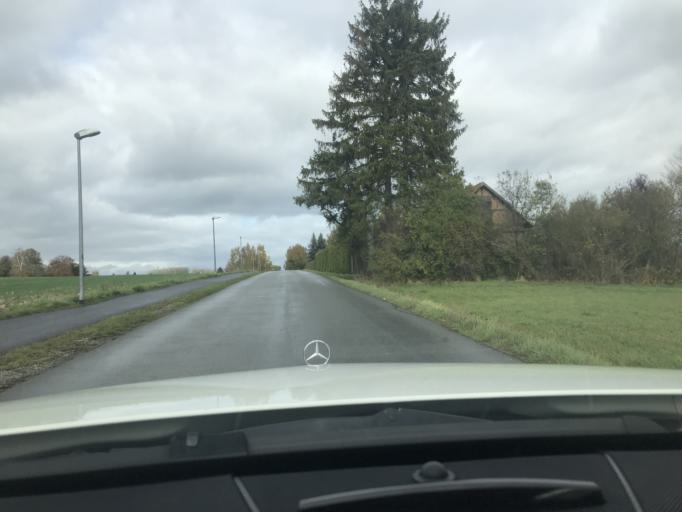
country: DE
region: Thuringia
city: Langula
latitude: 51.1569
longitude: 10.4207
